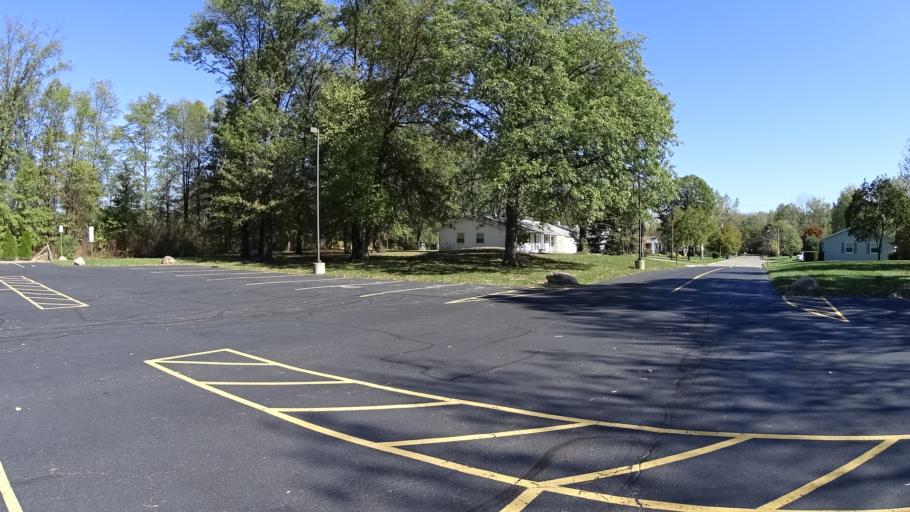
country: US
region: Ohio
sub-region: Lorain County
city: Amherst
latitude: 41.4127
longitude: -82.2071
